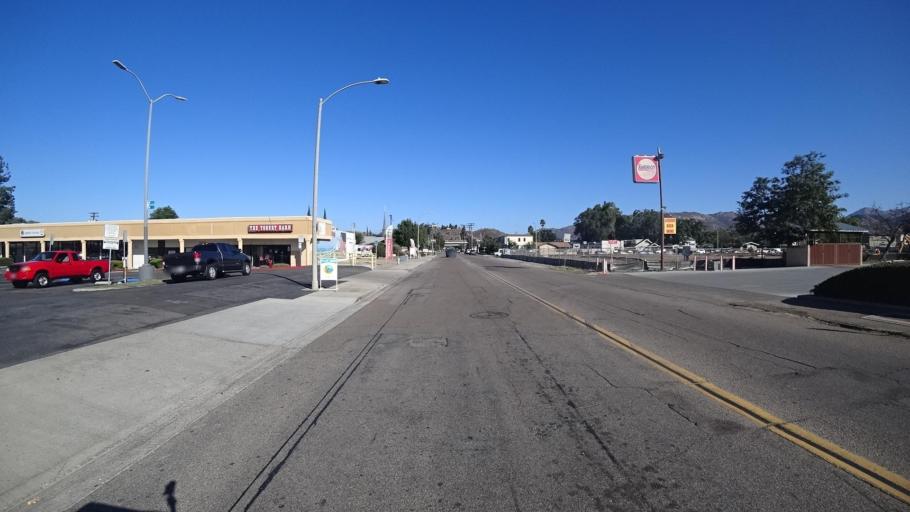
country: US
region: California
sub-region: San Diego County
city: Lakeside
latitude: 32.8573
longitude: -116.9255
